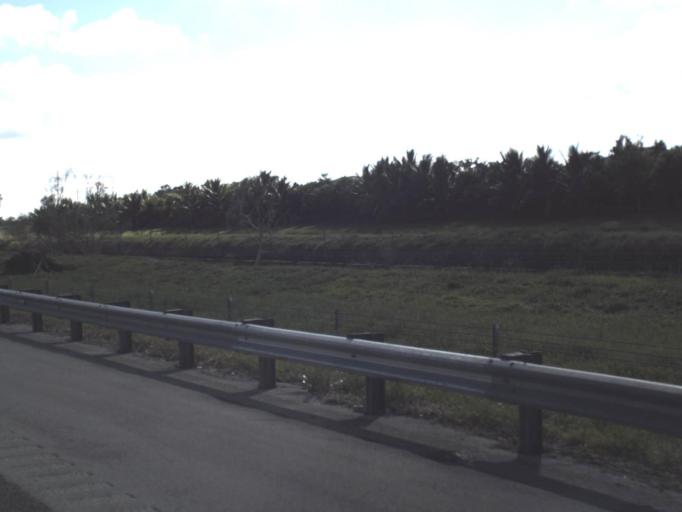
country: US
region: Florida
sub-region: Palm Beach County
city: Kings Point
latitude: 26.4270
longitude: -80.1720
